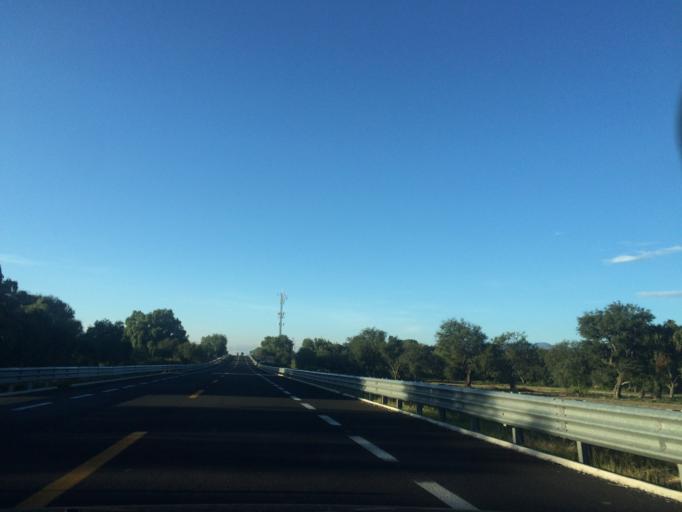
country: MX
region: Puebla
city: Santiago Miahuatlan
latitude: 18.5375
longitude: -97.4591
